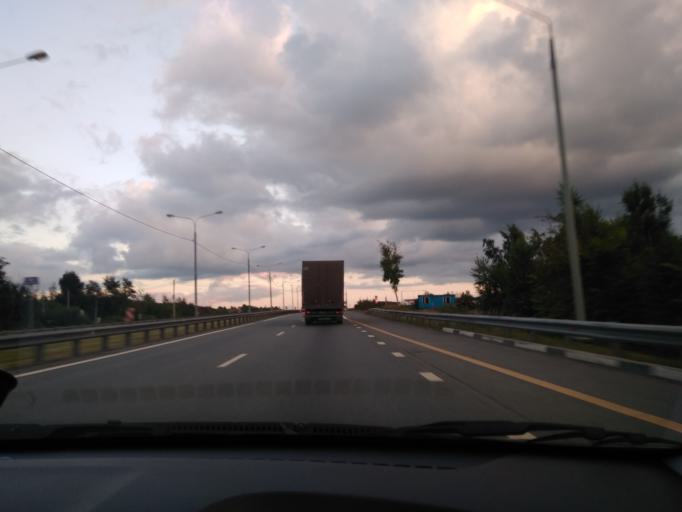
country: RU
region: Moskovskaya
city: Zhukovskiy
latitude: 55.5070
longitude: 38.1385
